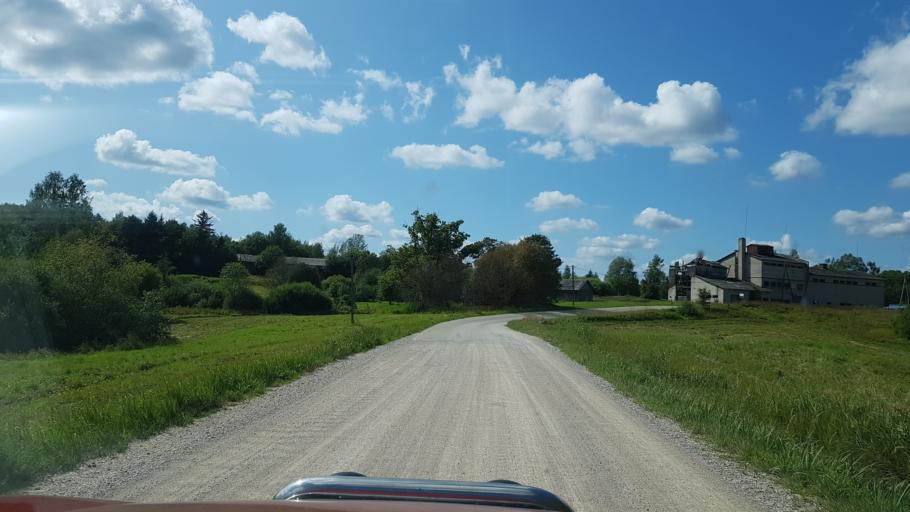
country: EE
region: Vorumaa
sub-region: Voru linn
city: Voru
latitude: 57.6323
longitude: 27.0938
